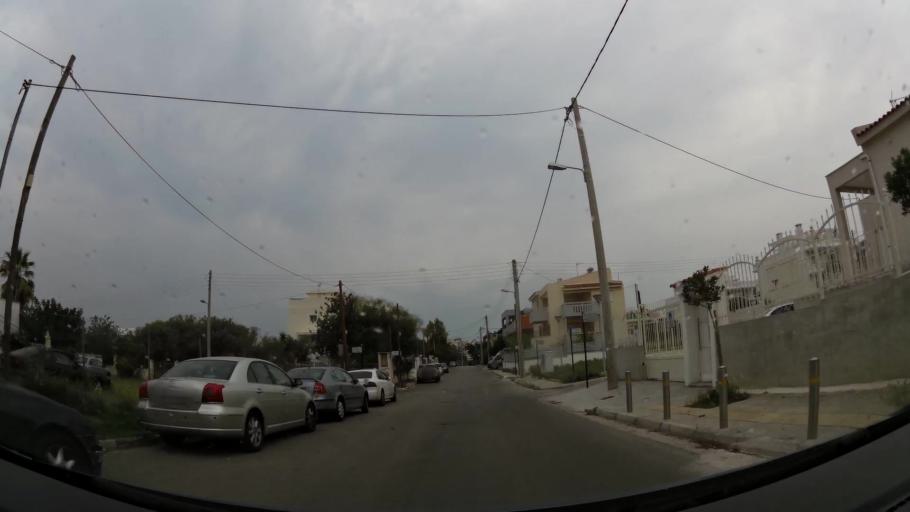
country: GR
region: Attica
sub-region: Nomarchia Athinas
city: Alimos
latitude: 37.9075
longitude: 23.7215
